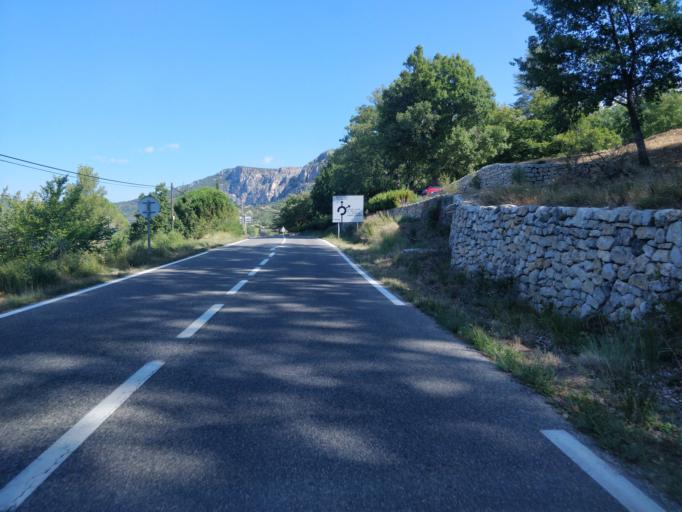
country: FR
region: Provence-Alpes-Cote d'Azur
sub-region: Departement des Alpes-de-Haute-Provence
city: Riez
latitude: 43.8257
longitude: 6.2248
